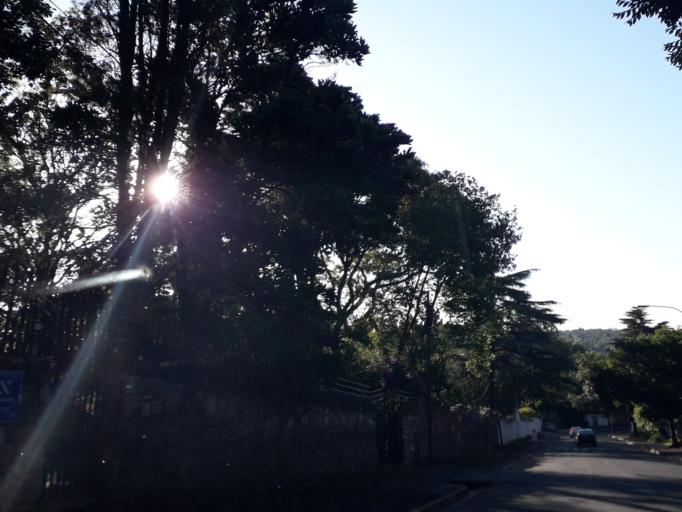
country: ZA
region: Gauteng
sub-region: City of Johannesburg Metropolitan Municipality
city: Johannesburg
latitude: -26.1820
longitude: 28.0237
